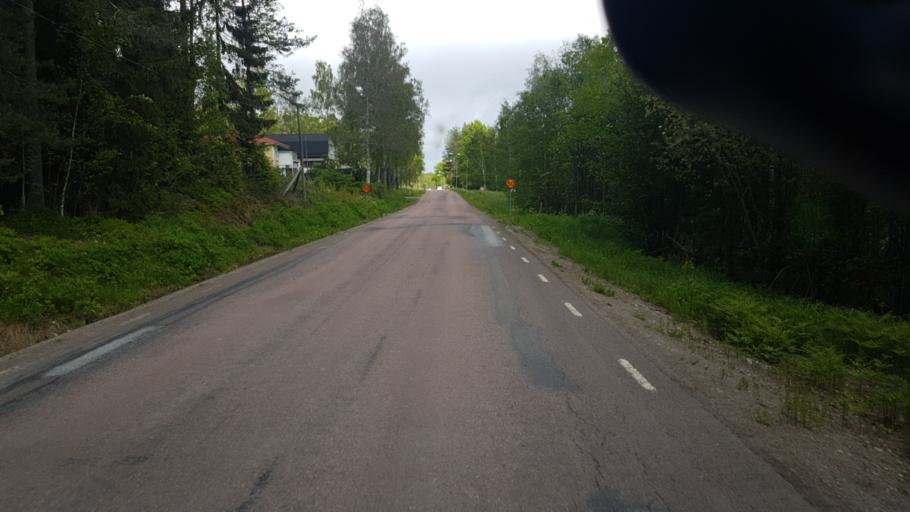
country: SE
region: Vaermland
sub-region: Arvika Kommun
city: Arvika
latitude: 59.6888
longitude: 12.4726
